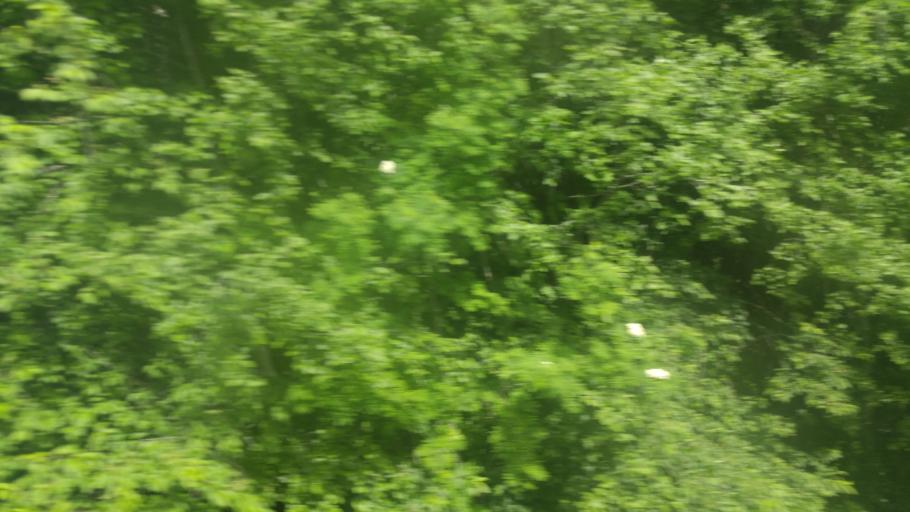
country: NO
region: Sor-Trondelag
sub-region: Klaebu
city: Klaebu
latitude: 62.9550
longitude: 10.6920
